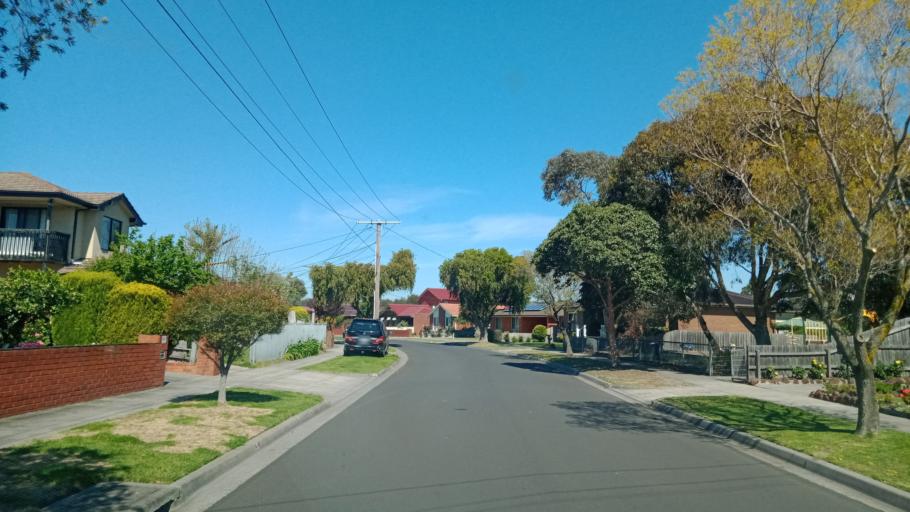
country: AU
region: Victoria
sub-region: Monash
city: Oakleigh South
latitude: -37.9379
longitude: 145.0827
